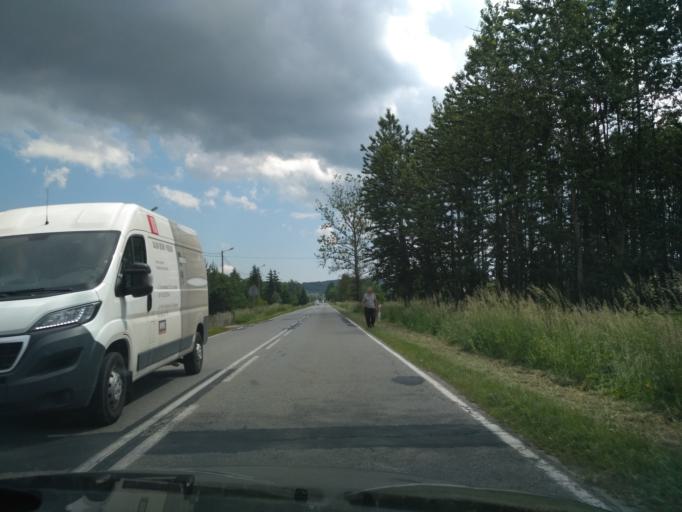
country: PL
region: Subcarpathian Voivodeship
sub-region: Powiat rzeszowski
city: Blazowa
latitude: 49.9264
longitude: 22.1289
